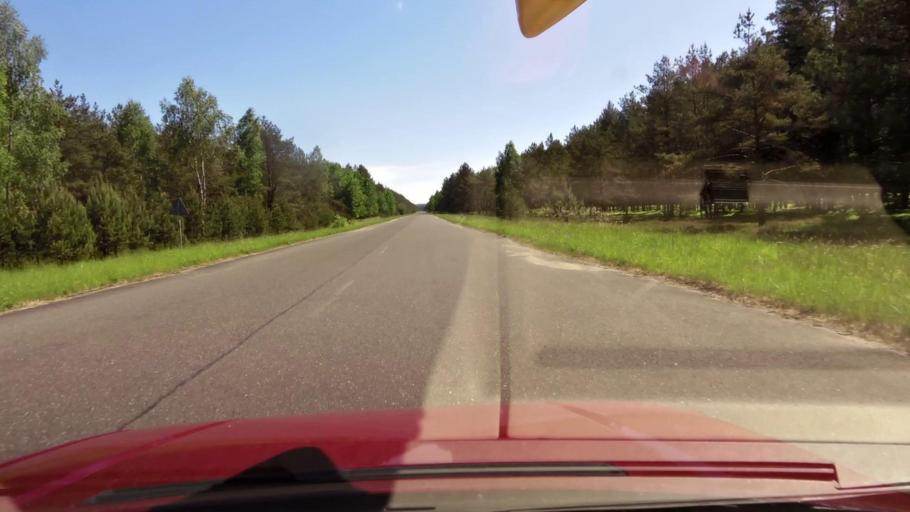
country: PL
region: West Pomeranian Voivodeship
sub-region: Powiat koszalinski
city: Bobolice
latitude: 54.0702
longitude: 16.5222
